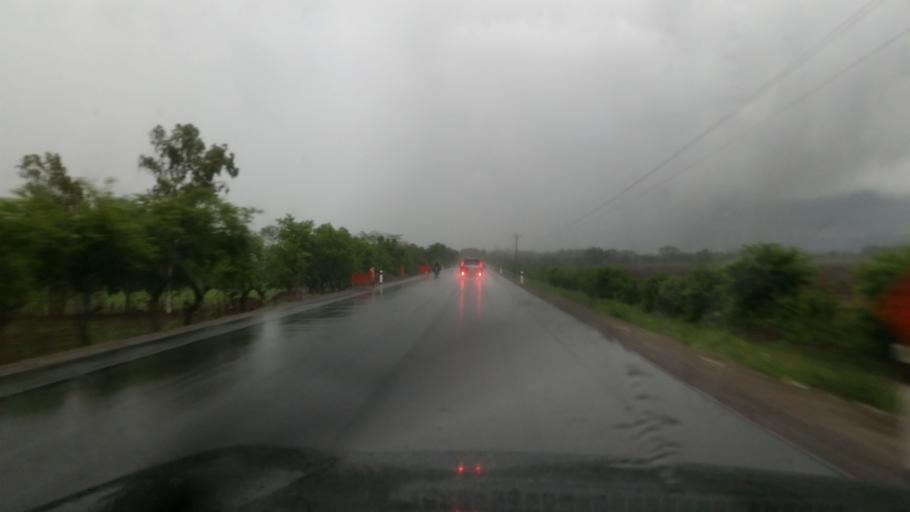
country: NI
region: Chinandega
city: Chichigalpa
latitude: 12.7719
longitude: -86.9181
